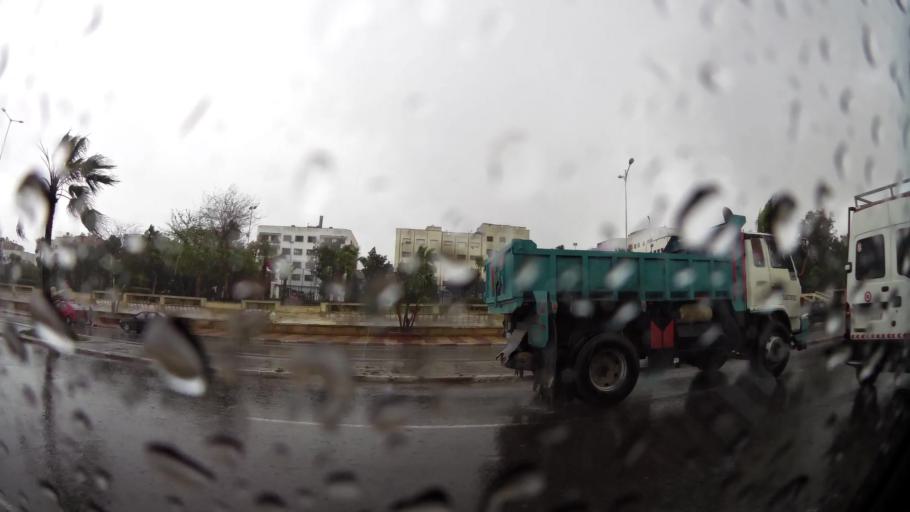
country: MA
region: Grand Casablanca
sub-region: Casablanca
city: Casablanca
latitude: 33.5387
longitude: -7.5777
